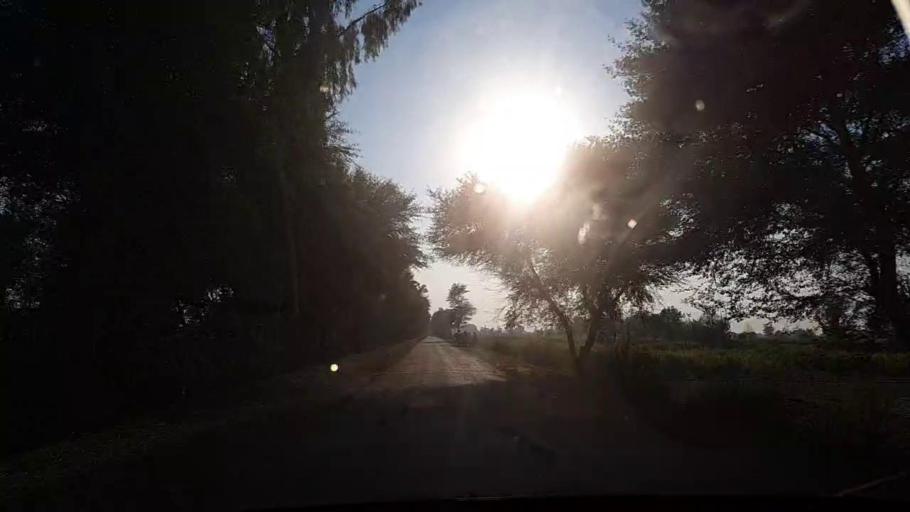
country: PK
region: Sindh
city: Sobhadero
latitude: 27.4171
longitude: 68.4020
